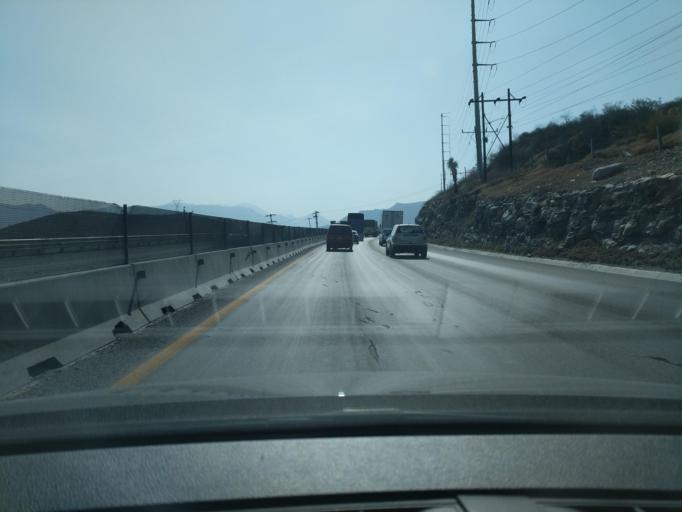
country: MX
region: Nuevo Leon
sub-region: Garcia
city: Los Parques
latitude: 25.7544
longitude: -100.5009
